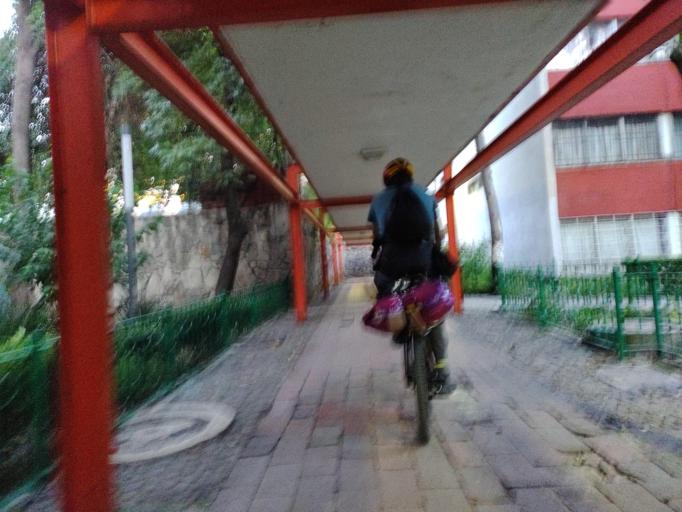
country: MX
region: Mexico City
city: Cuauhtemoc
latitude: 19.4517
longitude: -99.1400
